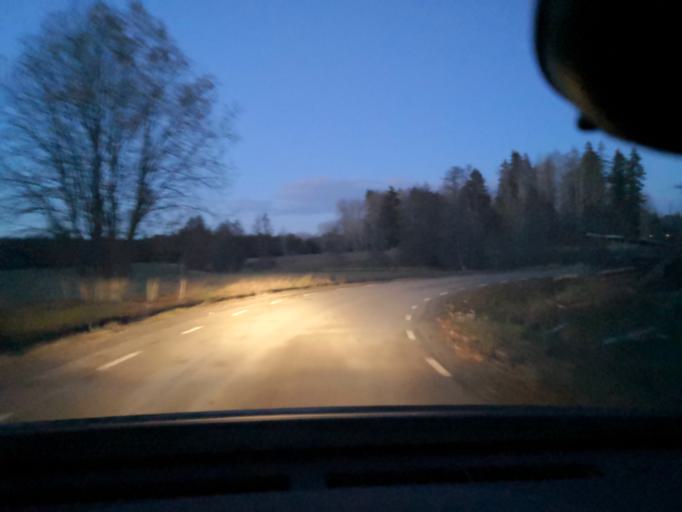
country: SE
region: Vaestmanland
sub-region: Sala Kommun
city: Sala
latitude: 59.8742
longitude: 16.7229
